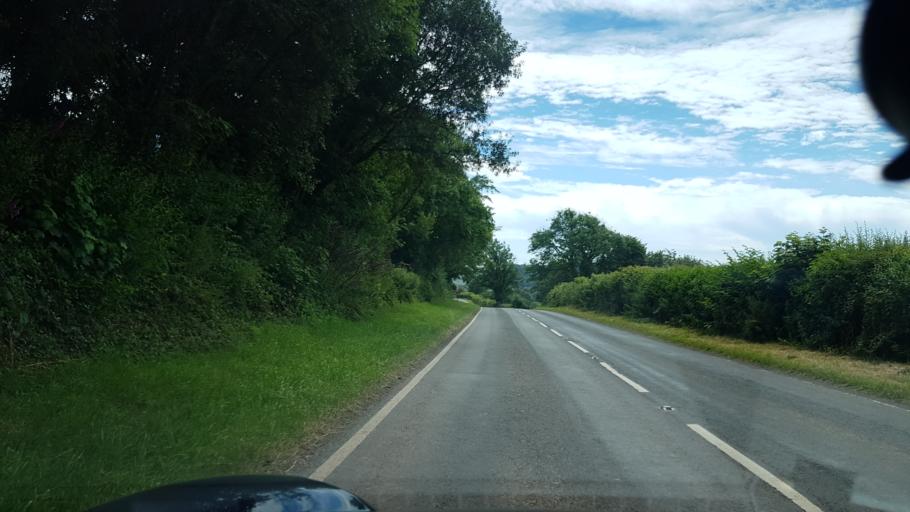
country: GB
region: Wales
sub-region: Carmarthenshire
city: Saint Clears
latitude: 51.7799
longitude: -4.4702
